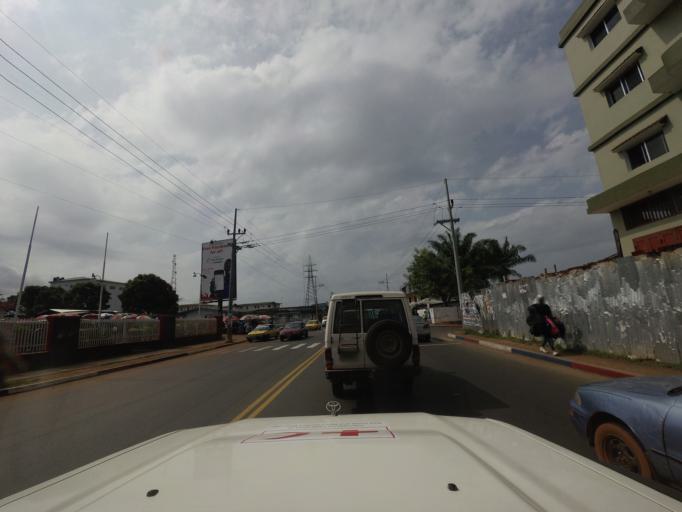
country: LR
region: Montserrado
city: Monrovia
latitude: 6.3075
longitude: -10.7974
